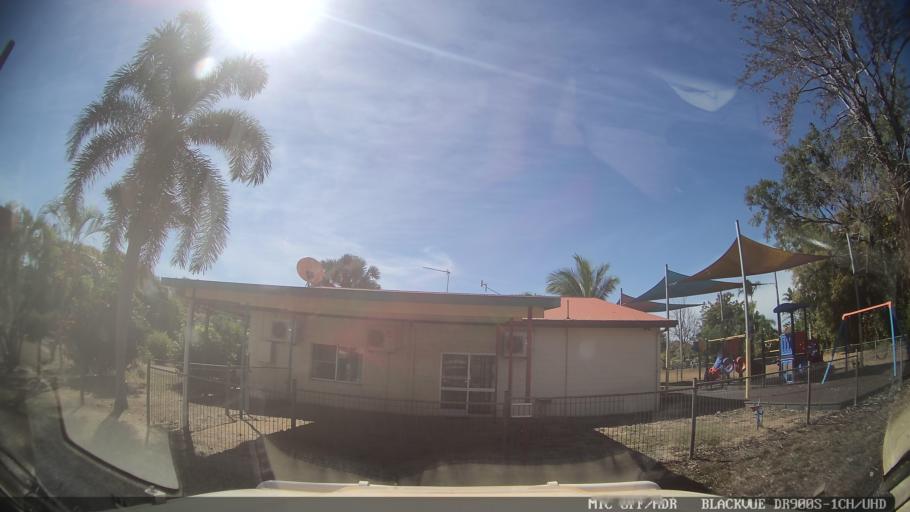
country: AU
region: Queensland
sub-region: Cook
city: Cooktown
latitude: -15.8589
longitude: 144.8552
